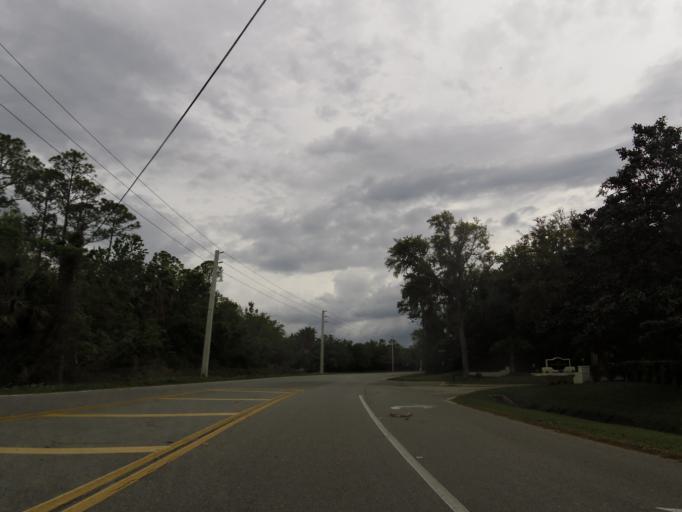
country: US
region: Florida
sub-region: Saint Johns County
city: Palm Valley
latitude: 30.1724
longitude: -81.3872
